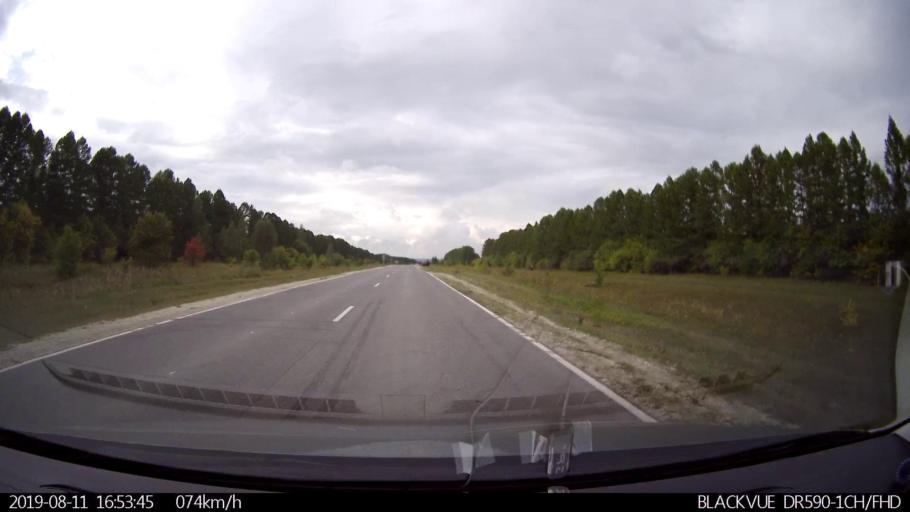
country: RU
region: Ulyanovsk
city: Mayna
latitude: 54.2658
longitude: 47.6691
